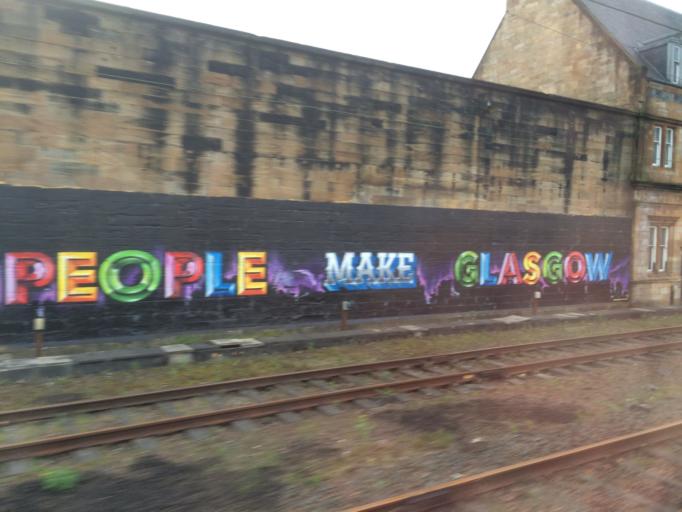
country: GB
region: Scotland
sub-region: Glasgow City
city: Glasgow
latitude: 55.8537
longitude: -4.2591
